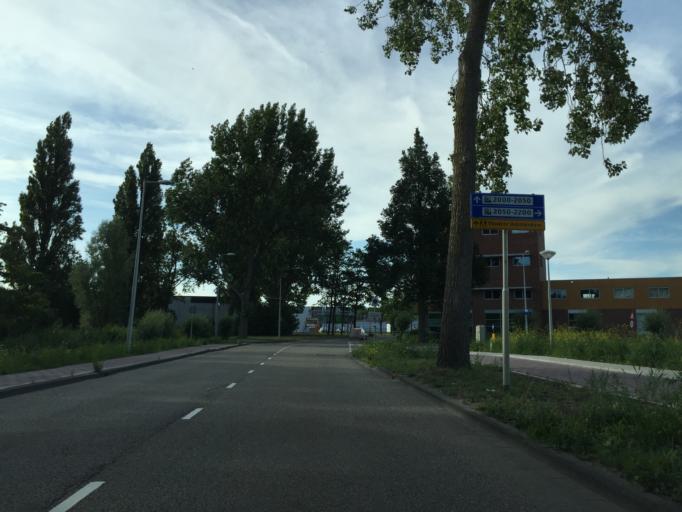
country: NL
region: North Holland
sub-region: Gemeente Amsterdam
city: Amsterdam
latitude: 52.3942
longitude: 4.8723
